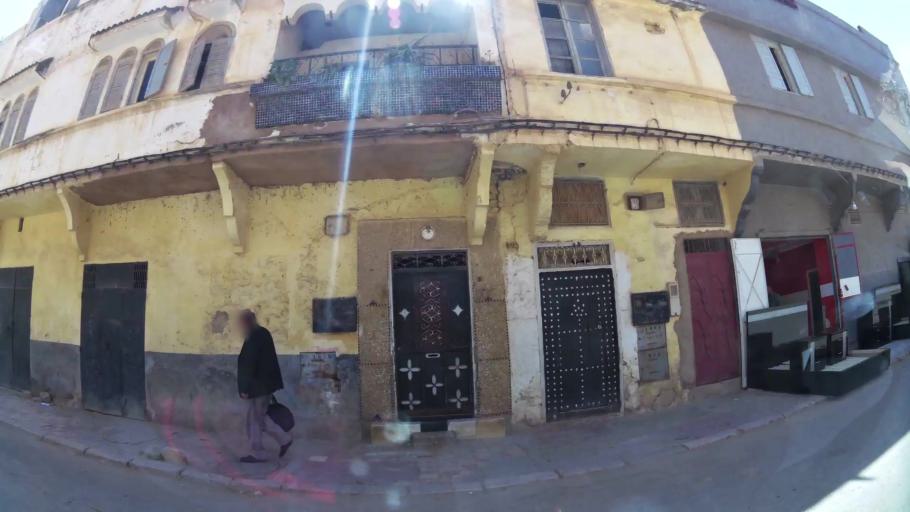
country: MA
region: Rabat-Sale-Zemmour-Zaer
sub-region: Khemisset
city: Khemisset
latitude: 33.8284
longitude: -6.0749
